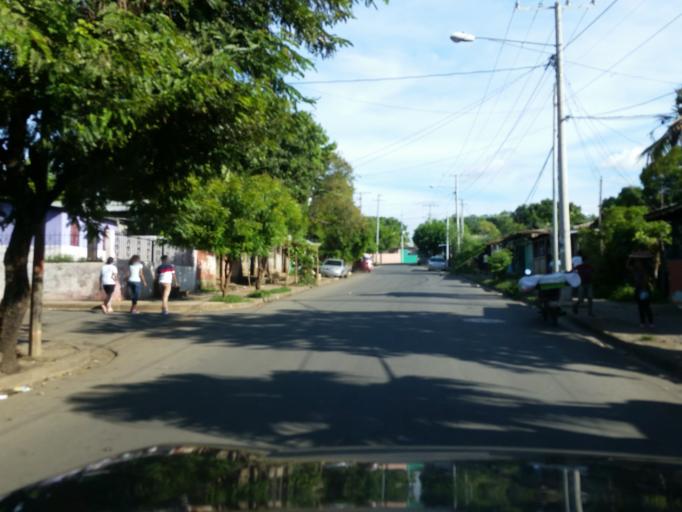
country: NI
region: Managua
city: Managua
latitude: 12.1045
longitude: -86.2229
